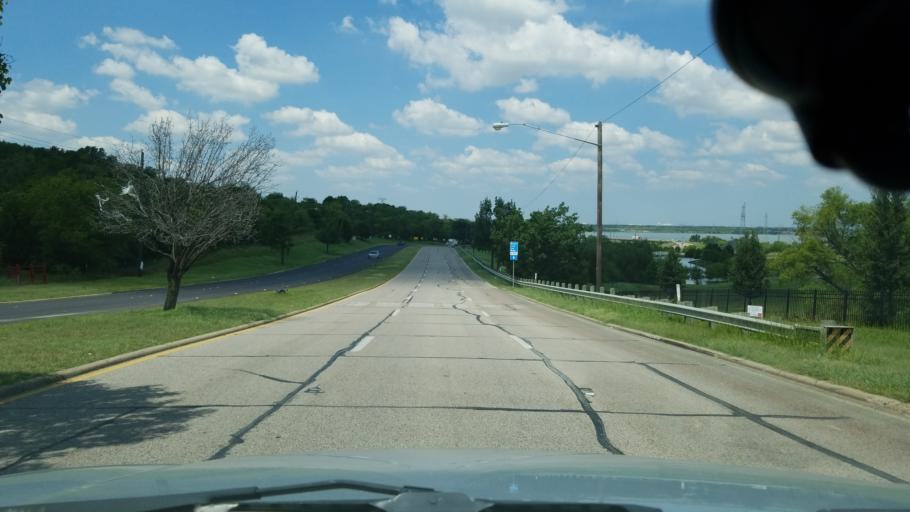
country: US
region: Texas
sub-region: Dallas County
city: Grand Prairie
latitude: 32.7058
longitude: -96.9475
